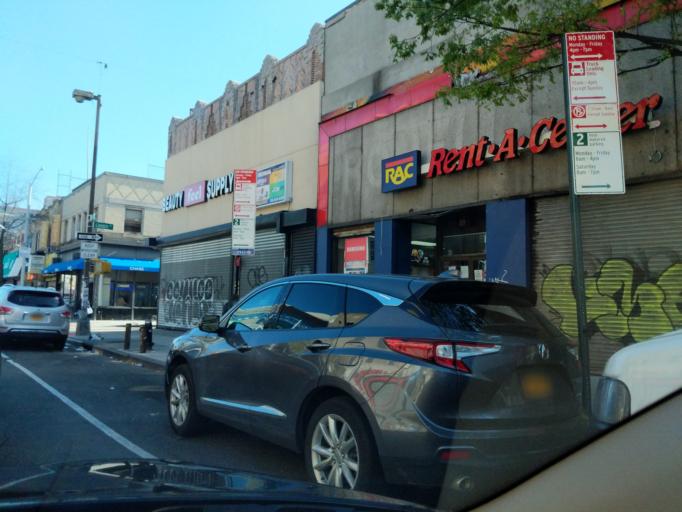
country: US
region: New York
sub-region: Kings County
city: Brooklyn
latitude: 40.6695
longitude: -73.9310
